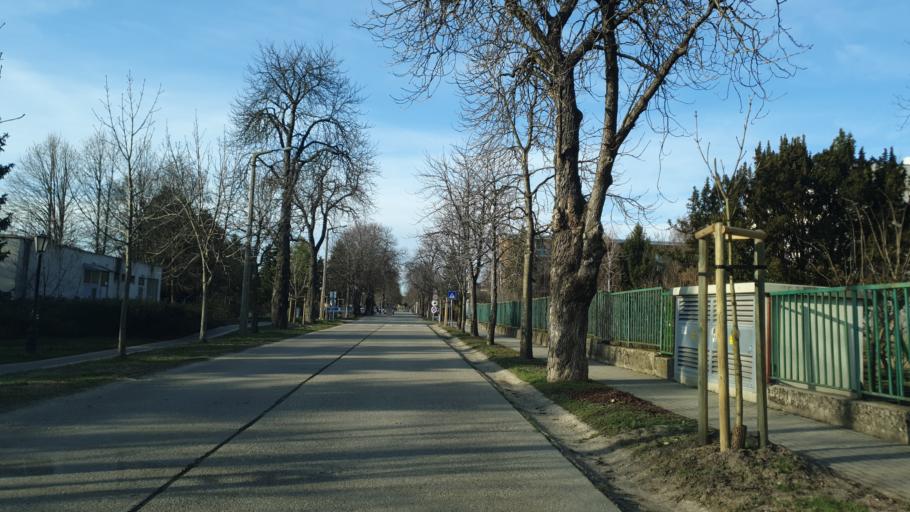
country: HU
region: Fejer
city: Etyek
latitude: 47.4990
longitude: 18.7529
